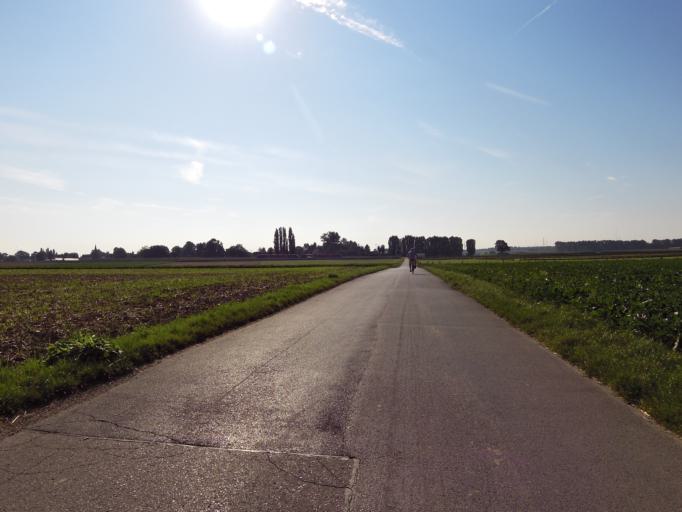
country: DE
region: North Rhine-Westphalia
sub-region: Regierungsbezirk Koln
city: Alsdorf
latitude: 50.8365
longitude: 6.1968
